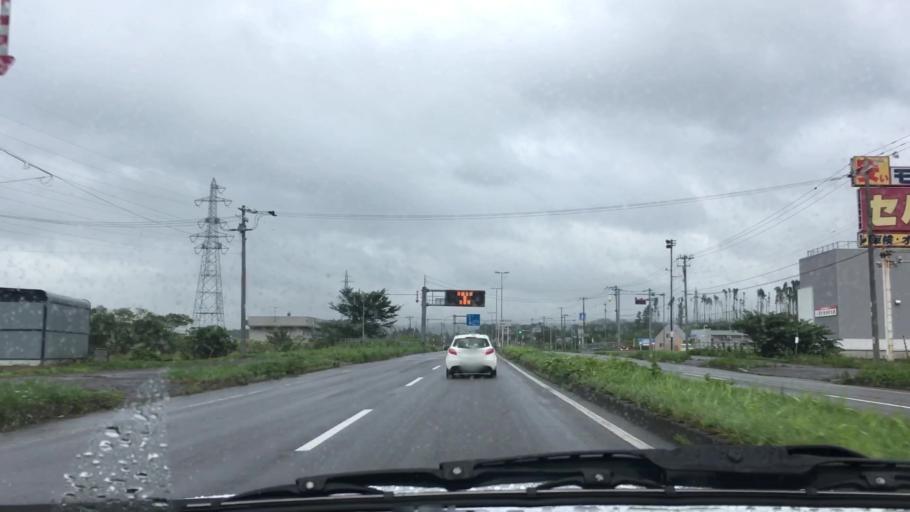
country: JP
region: Hokkaido
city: Nanae
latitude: 42.2477
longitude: 140.2881
